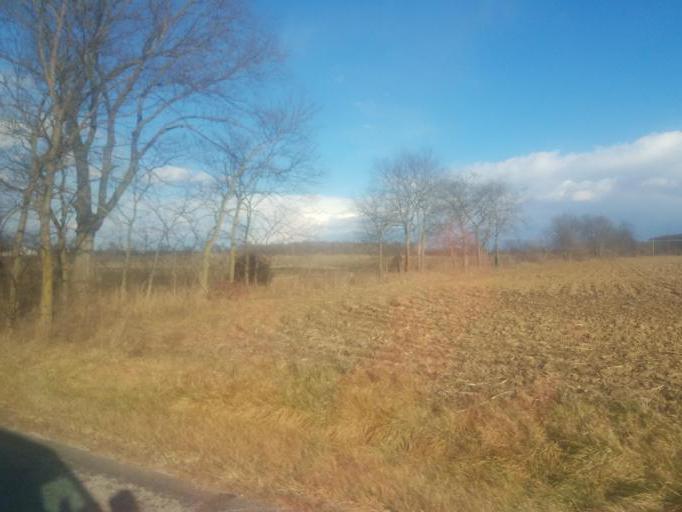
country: US
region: Ohio
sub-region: Marion County
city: Prospect
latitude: 40.3936
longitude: -83.1450
